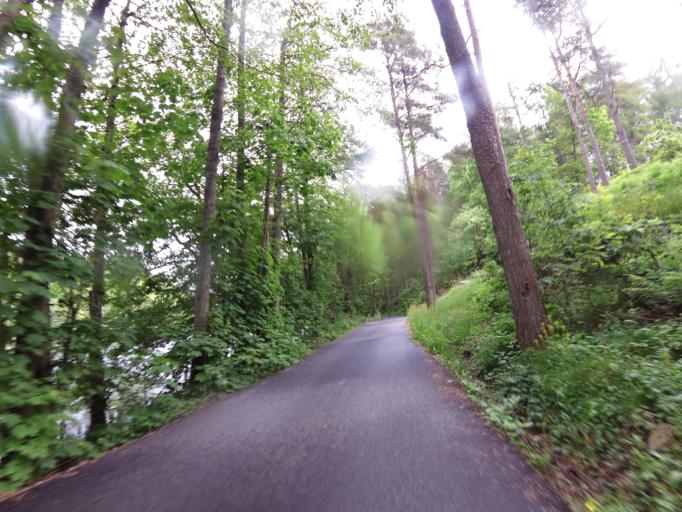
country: NO
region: Vest-Agder
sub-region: Mandal
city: Mandal
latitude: 58.0114
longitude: 7.5230
